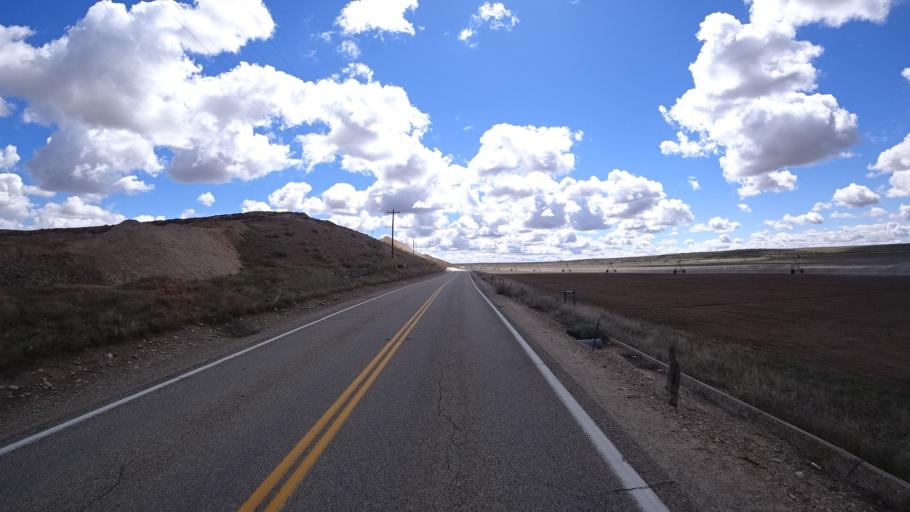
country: US
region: Idaho
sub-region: Ada County
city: Garden City
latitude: 43.4889
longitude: -116.2611
